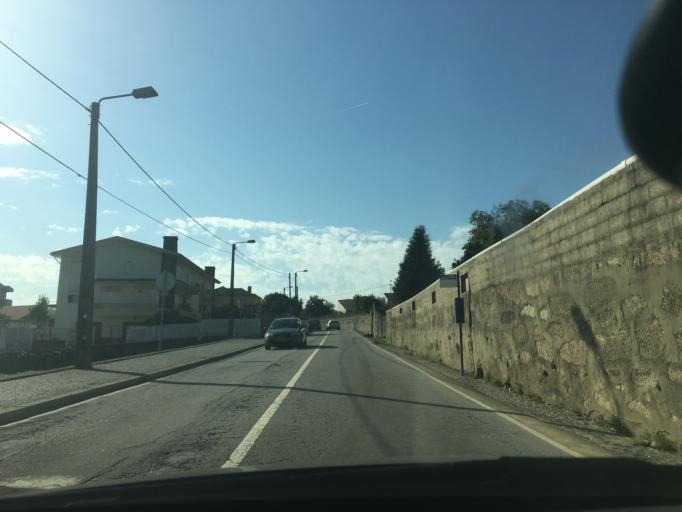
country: PT
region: Porto
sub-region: Maia
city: Gemunde
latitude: 41.2478
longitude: -8.6429
